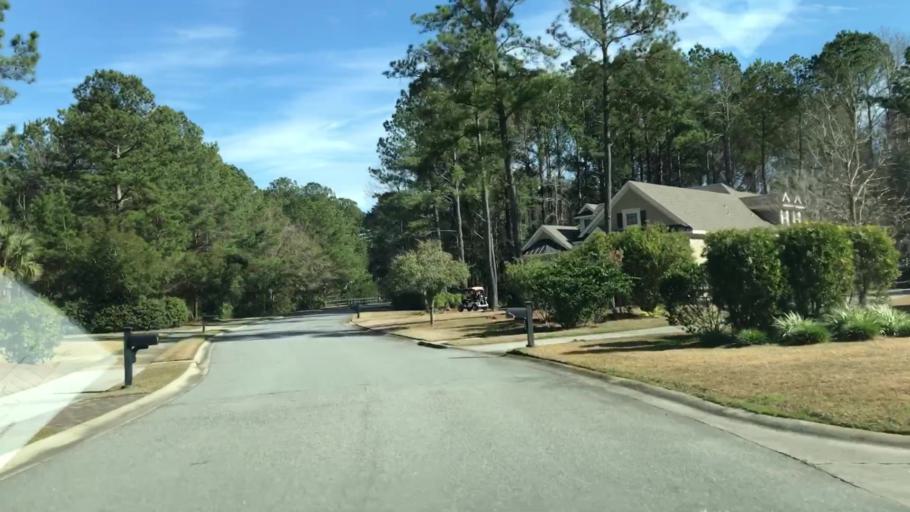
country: US
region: South Carolina
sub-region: Beaufort County
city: Bluffton
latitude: 32.2525
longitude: -80.9218
